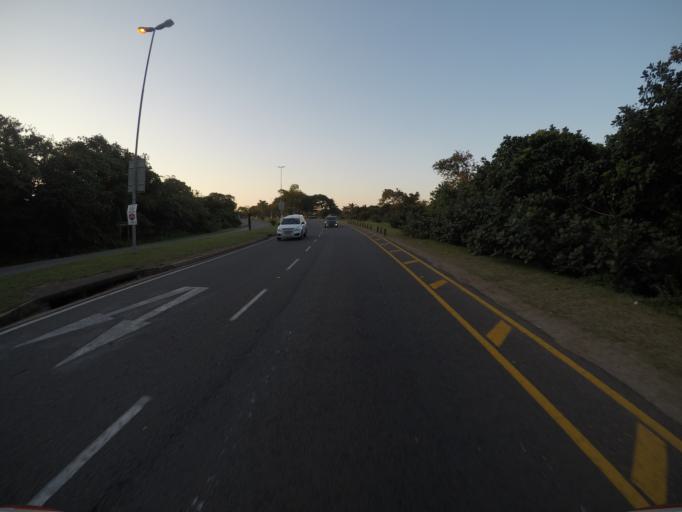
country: ZA
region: KwaZulu-Natal
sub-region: uThungulu District Municipality
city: Richards Bay
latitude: -28.7683
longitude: 32.0599
